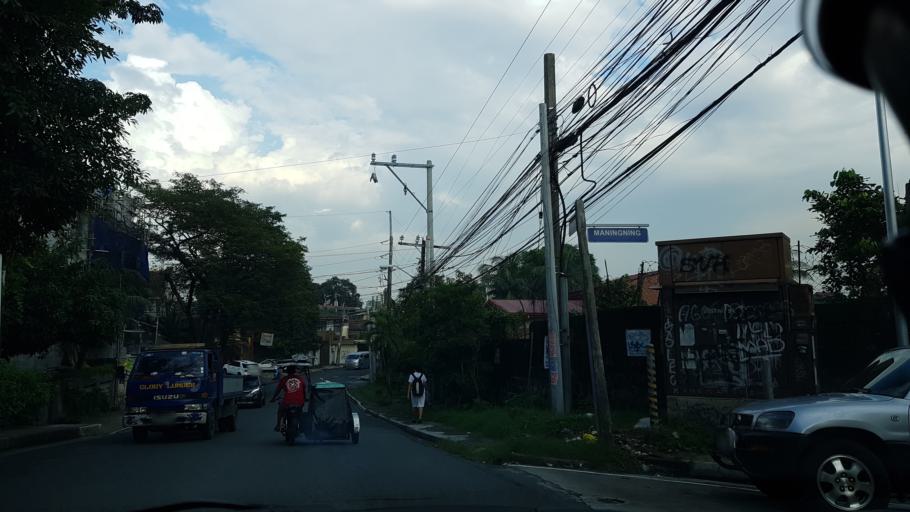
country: PH
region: Metro Manila
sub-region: Quezon City
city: Quezon City
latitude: 14.6394
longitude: 121.0569
